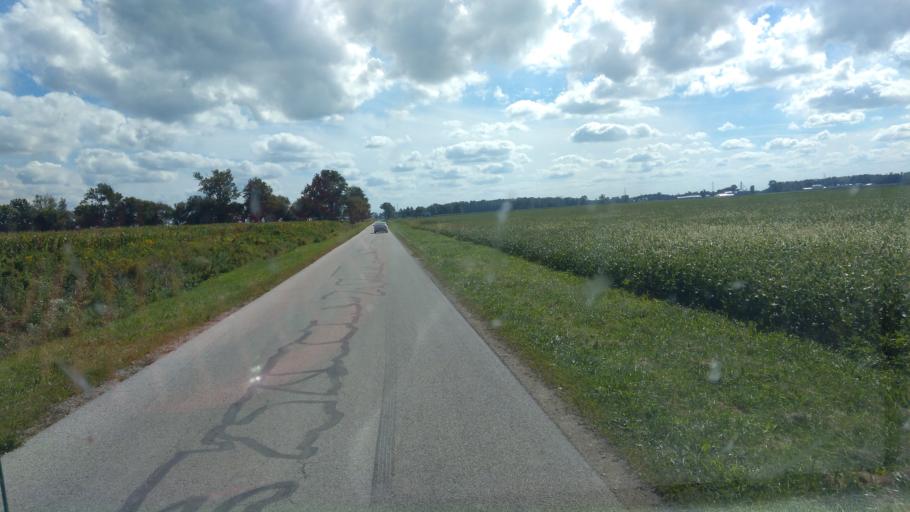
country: US
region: Ohio
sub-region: Ottawa County
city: Port Clinton
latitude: 41.4078
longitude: -82.8825
